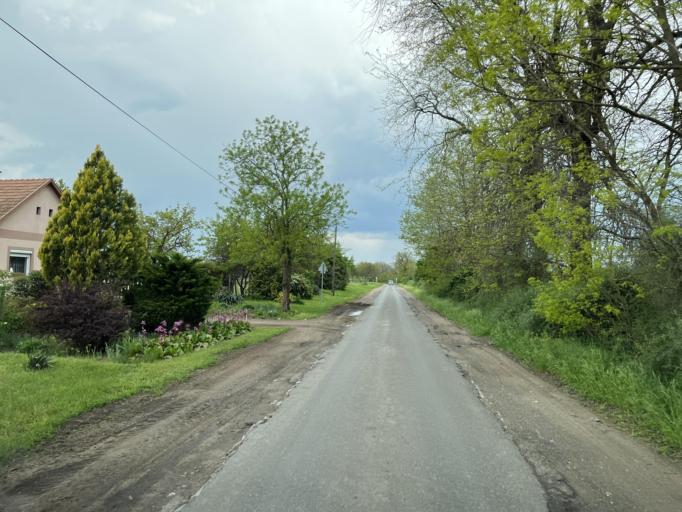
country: HU
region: Pest
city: Nagykoros
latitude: 47.0116
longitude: 19.7950
